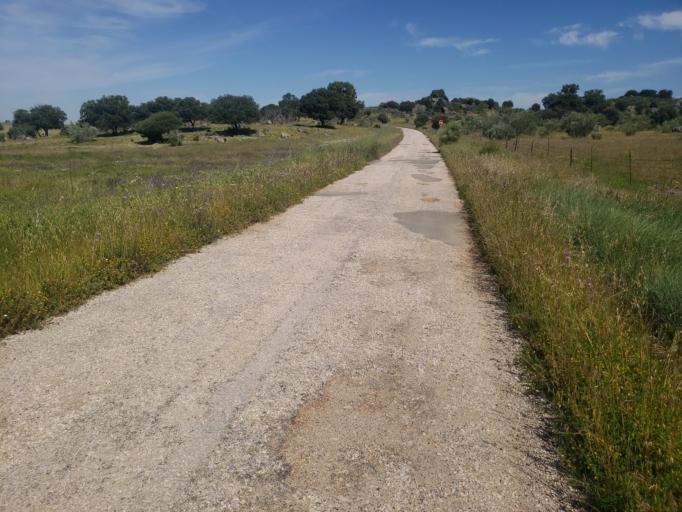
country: ES
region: Extremadura
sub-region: Provincia de Caceres
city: Malpartida de Caceres
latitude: 39.4163
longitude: -6.5011
